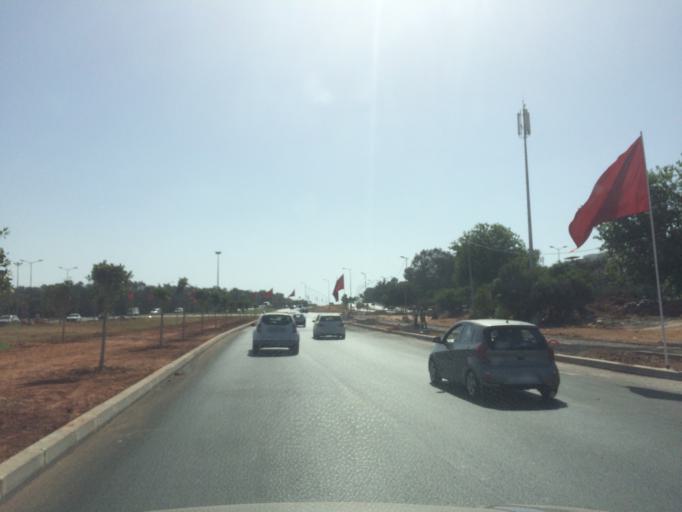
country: MA
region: Rabat-Sale-Zemmour-Zaer
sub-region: Skhirate-Temara
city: Temara
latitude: 33.9674
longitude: -6.8863
